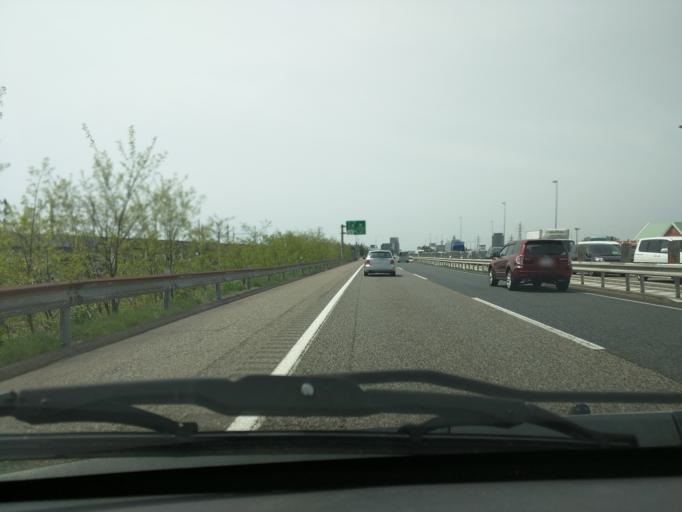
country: JP
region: Niigata
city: Tsubame
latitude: 37.6562
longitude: 138.9419
